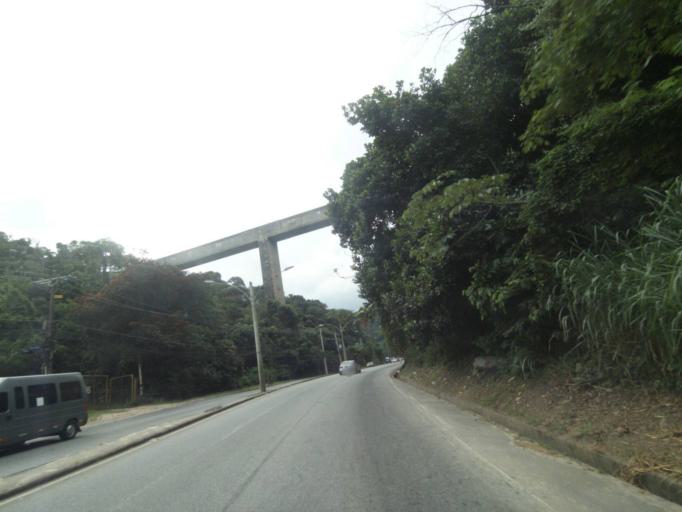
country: BR
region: Rio de Janeiro
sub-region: Sao Joao De Meriti
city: Sao Joao de Meriti
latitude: -22.9038
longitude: -43.3807
